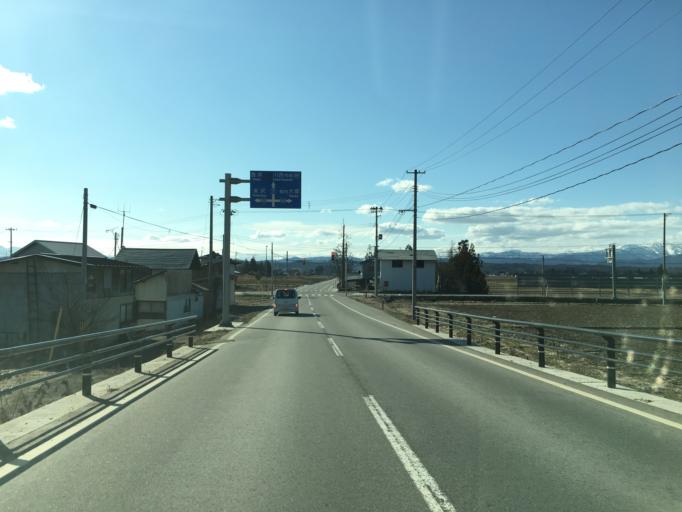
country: JP
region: Yamagata
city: Nagai
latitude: 38.0100
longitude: 140.0789
